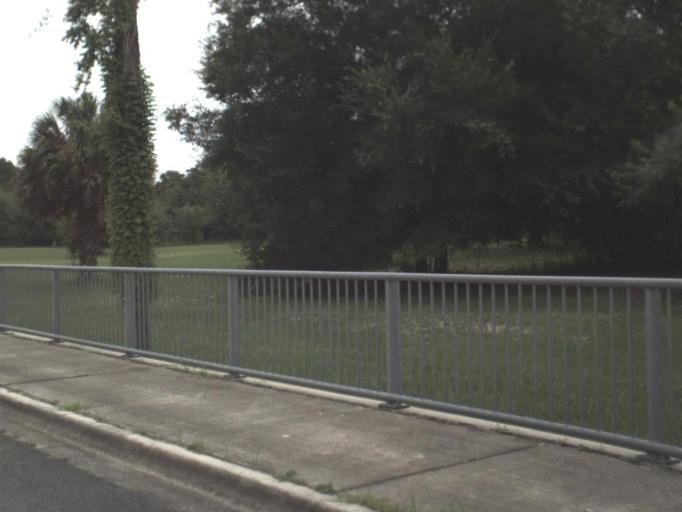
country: US
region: Florida
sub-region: Citrus County
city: Inverness
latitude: 28.8405
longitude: -82.2979
